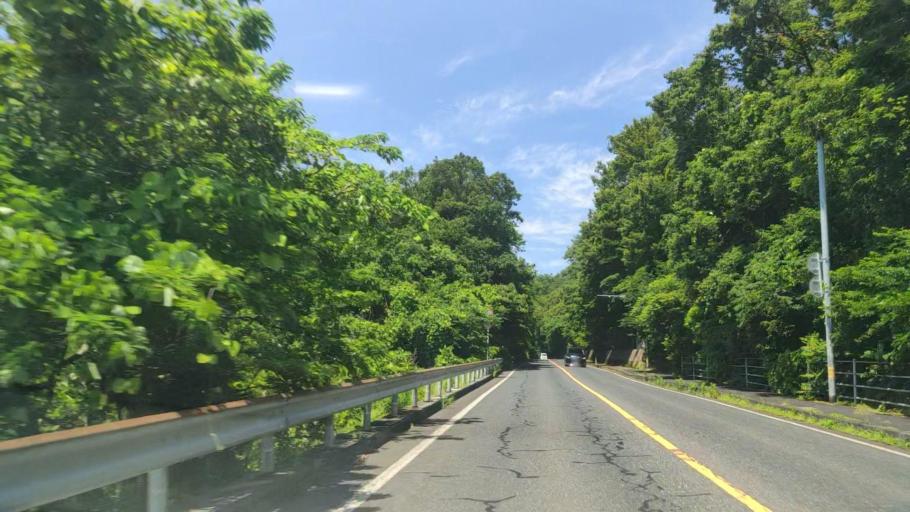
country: JP
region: Tottori
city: Tottori
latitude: 35.5260
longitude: 134.2303
